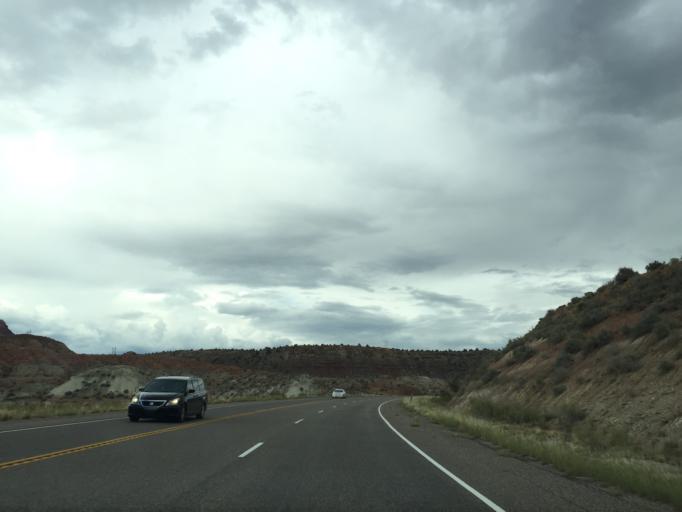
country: US
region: Utah
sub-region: Washington County
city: Hildale
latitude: 37.1709
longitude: -113.0709
